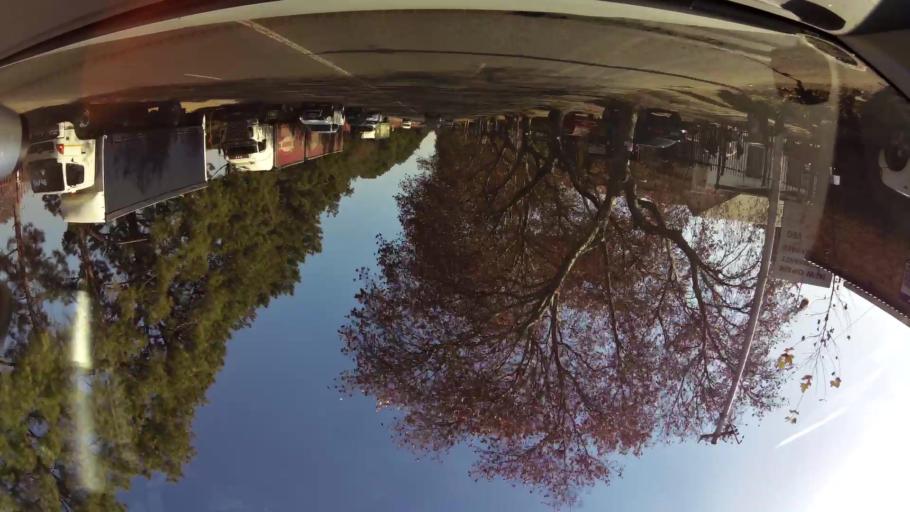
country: ZA
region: Gauteng
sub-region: City of Tshwane Metropolitan Municipality
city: Pretoria
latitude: -25.7481
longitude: 28.1637
